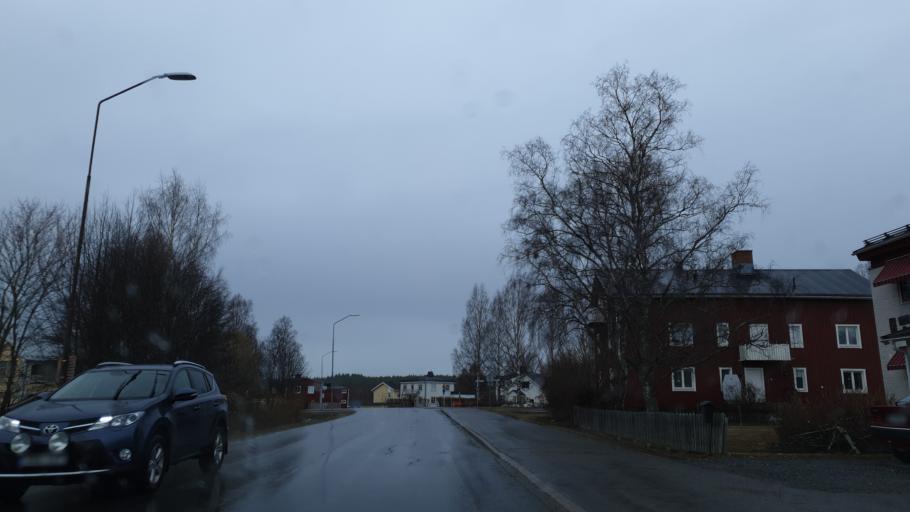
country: SE
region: Vaesterbotten
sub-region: Skelleftea Kommun
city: Kage
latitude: 64.8374
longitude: 20.9842
